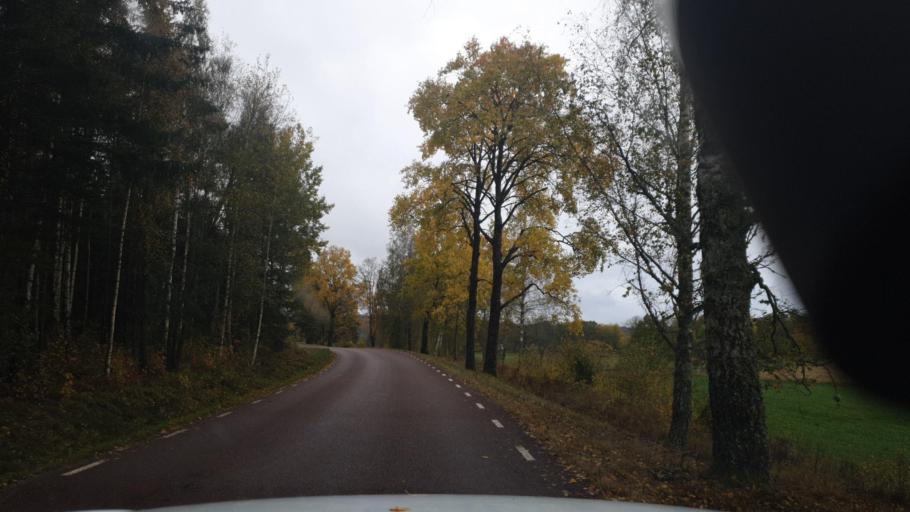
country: SE
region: Vaermland
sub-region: Karlstads Kommun
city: Valberg
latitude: 59.4394
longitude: 13.0896
